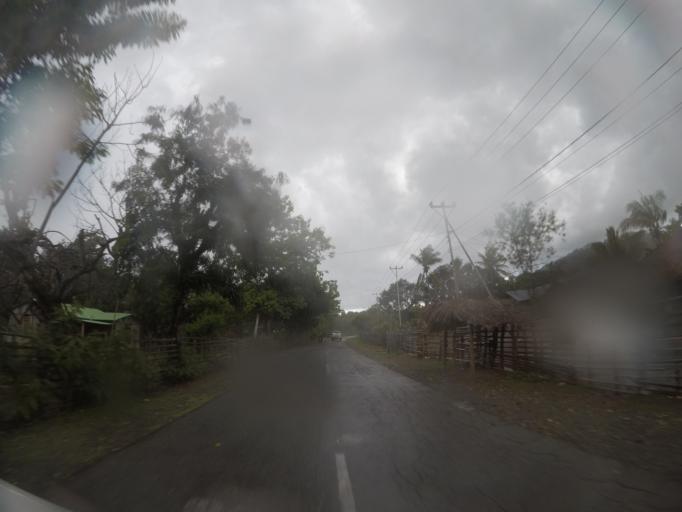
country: ID
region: East Nusa Tenggara
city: Atambua
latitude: -8.9620
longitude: 124.9911
